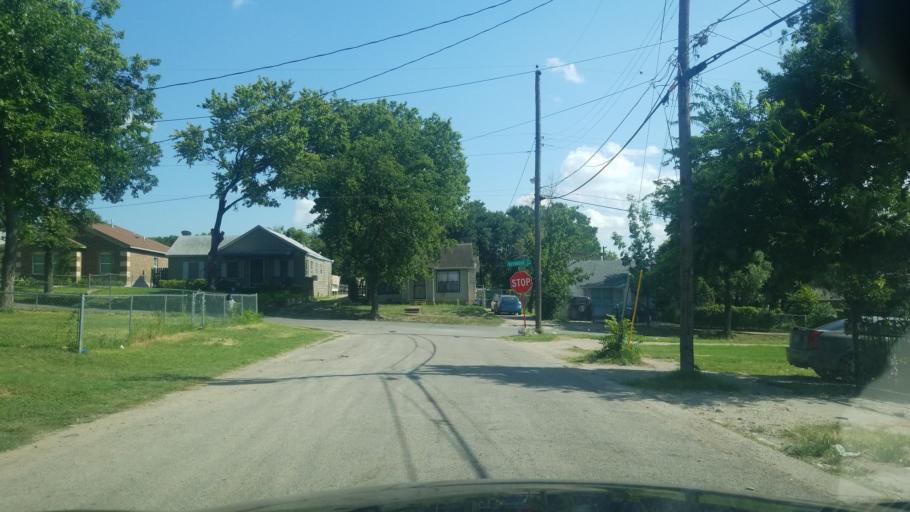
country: US
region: Texas
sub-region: Dallas County
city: Dallas
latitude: 32.7275
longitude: -96.8077
